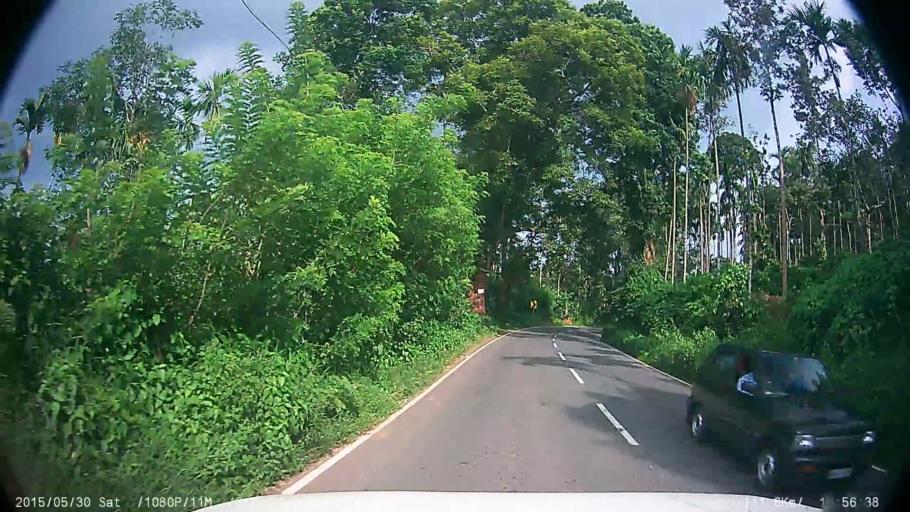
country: IN
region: Kerala
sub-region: Wayanad
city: Kalpetta
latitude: 11.6585
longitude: 76.0863
